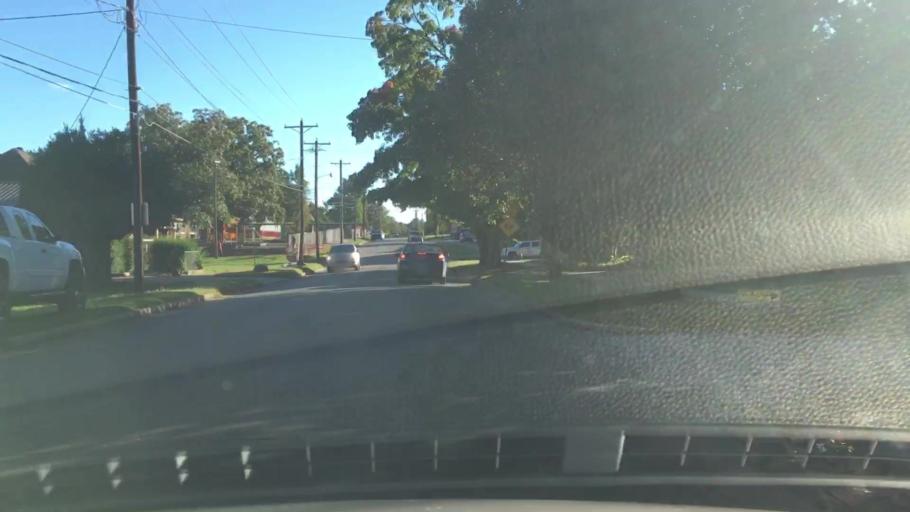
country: US
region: Oklahoma
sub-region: Cherokee County
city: Tahlequah
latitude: 35.9111
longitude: -94.9736
